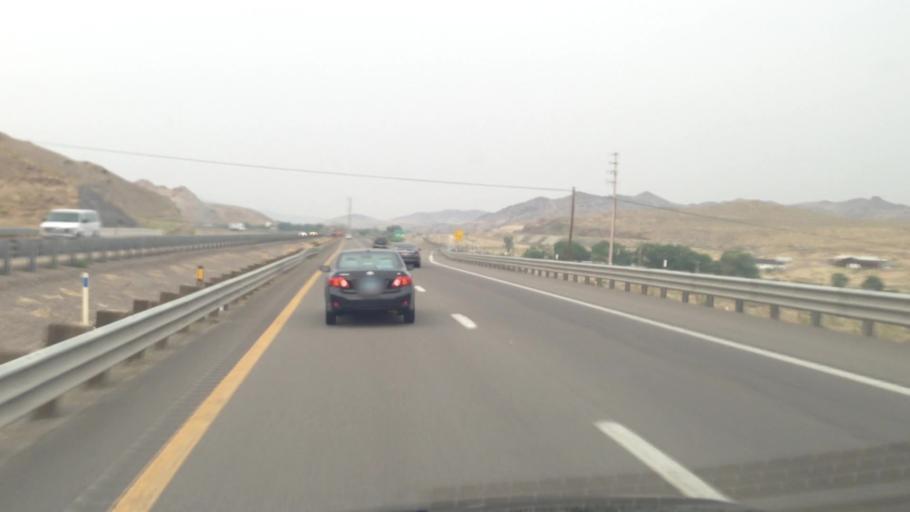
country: US
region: Nevada
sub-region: Lyon County
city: Fernley
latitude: 39.5901
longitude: -119.3741
